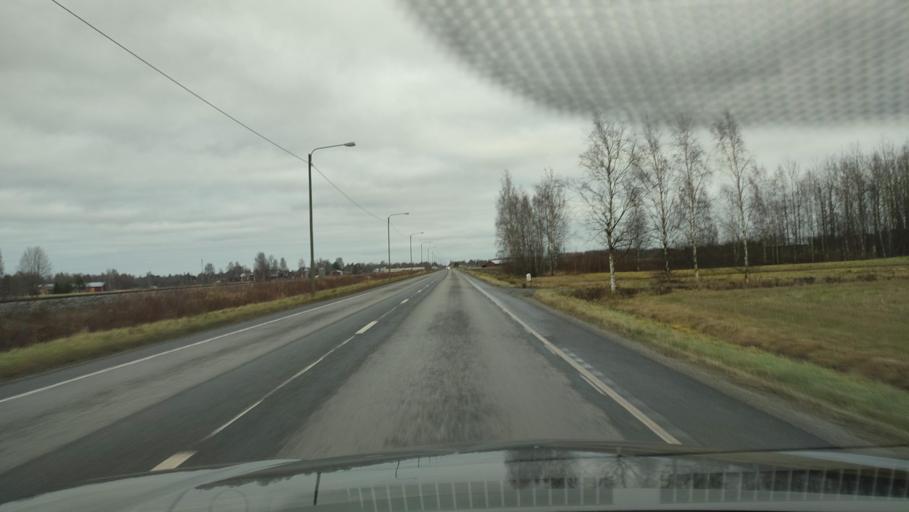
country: FI
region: Southern Ostrobothnia
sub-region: Seinaejoki
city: Ilmajoki
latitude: 62.7180
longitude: 22.5584
